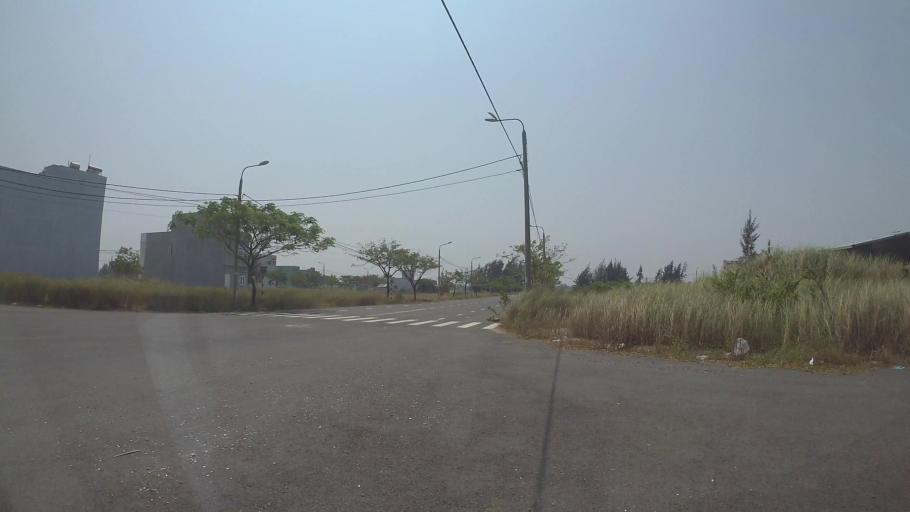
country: VN
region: Da Nang
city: Ngu Hanh Son
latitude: 15.9862
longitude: 108.2678
